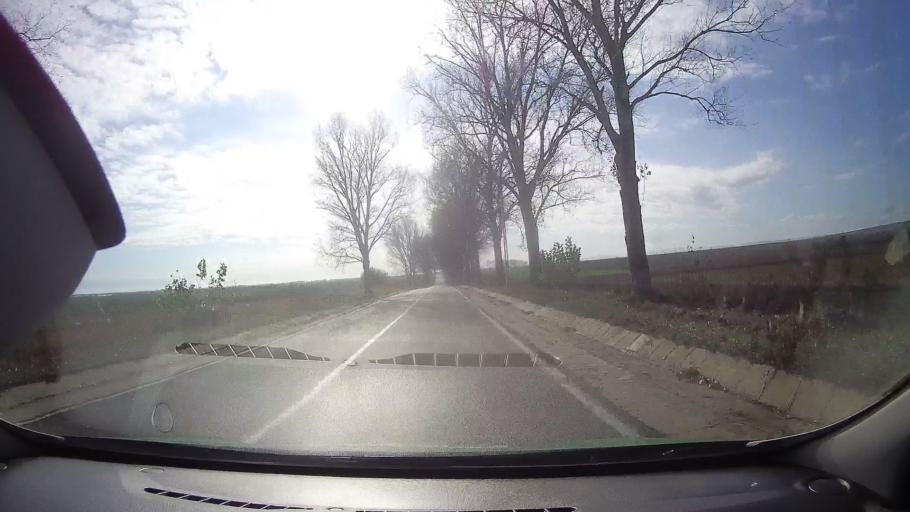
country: RO
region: Tulcea
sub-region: Comuna Valea Nucarilor
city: Agighiol
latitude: 45.0038
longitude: 28.8855
